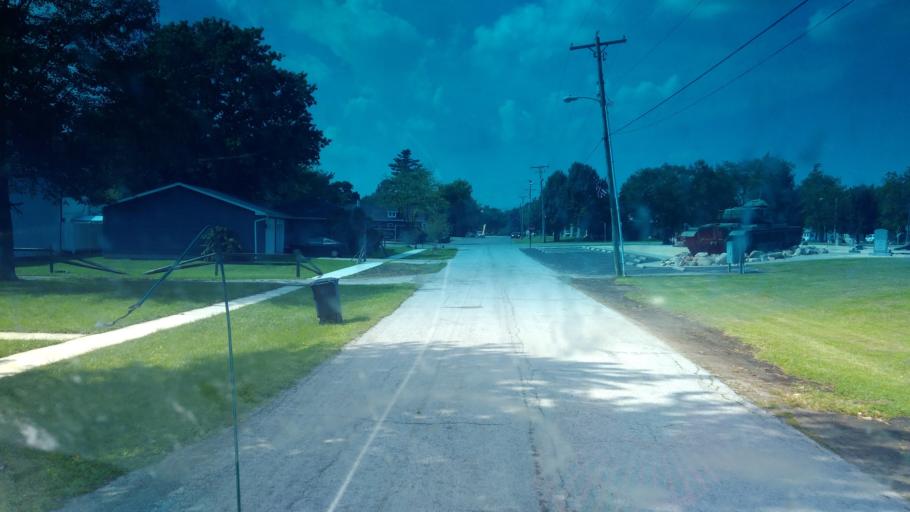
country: US
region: Ohio
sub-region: Hardin County
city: Ada
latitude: 40.7089
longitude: -83.9199
